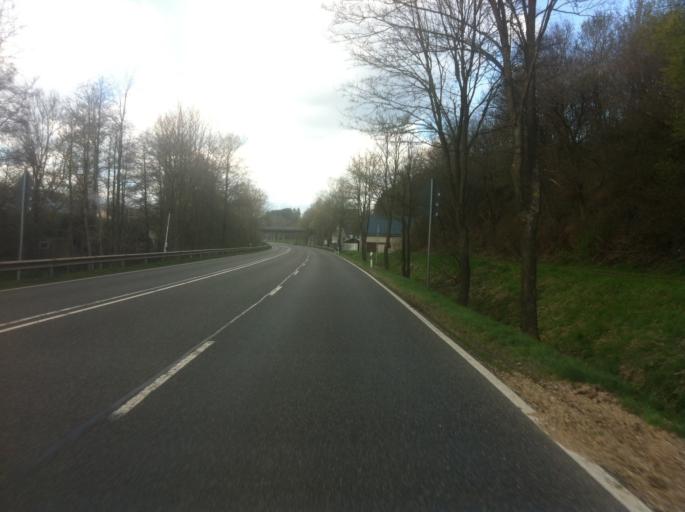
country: DE
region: Rheinland-Pfalz
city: Olzheim
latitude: 50.2713
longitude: 6.4580
